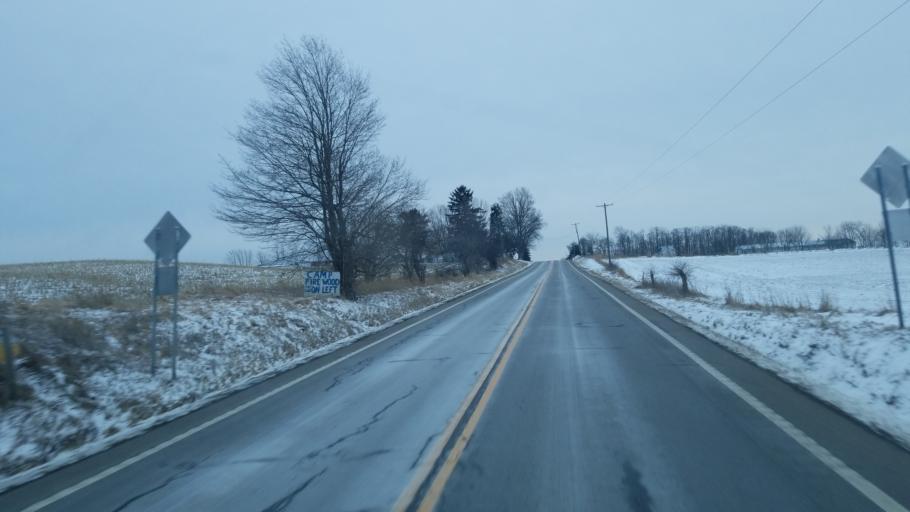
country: US
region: Ohio
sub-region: Ashland County
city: Loudonville
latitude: 40.7370
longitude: -82.2409
